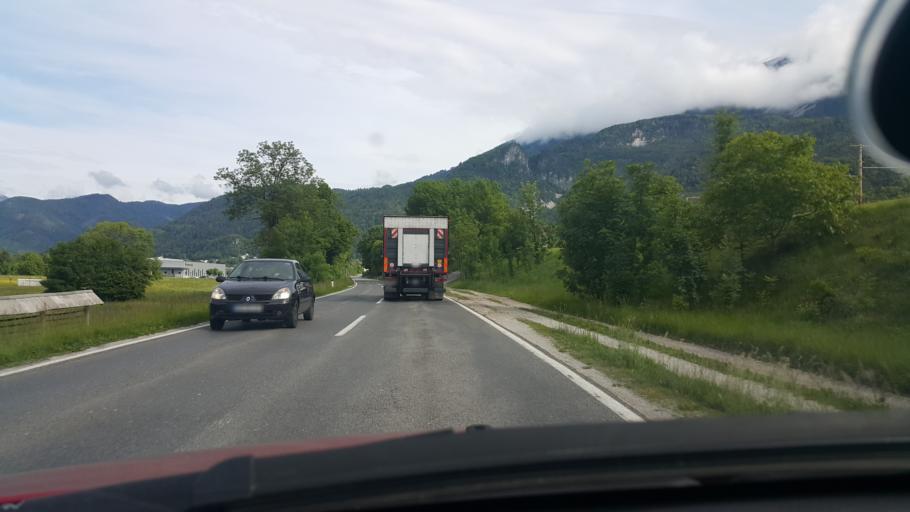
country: SI
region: Zirovnica
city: Zirovnica
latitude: 46.3980
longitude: 14.1367
